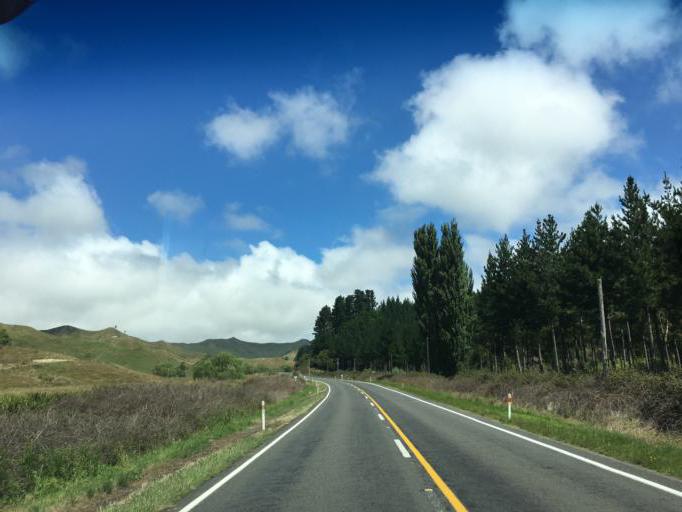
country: NZ
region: Hawke's Bay
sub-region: Wairoa District
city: Wairoa
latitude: -39.0392
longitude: 177.3101
